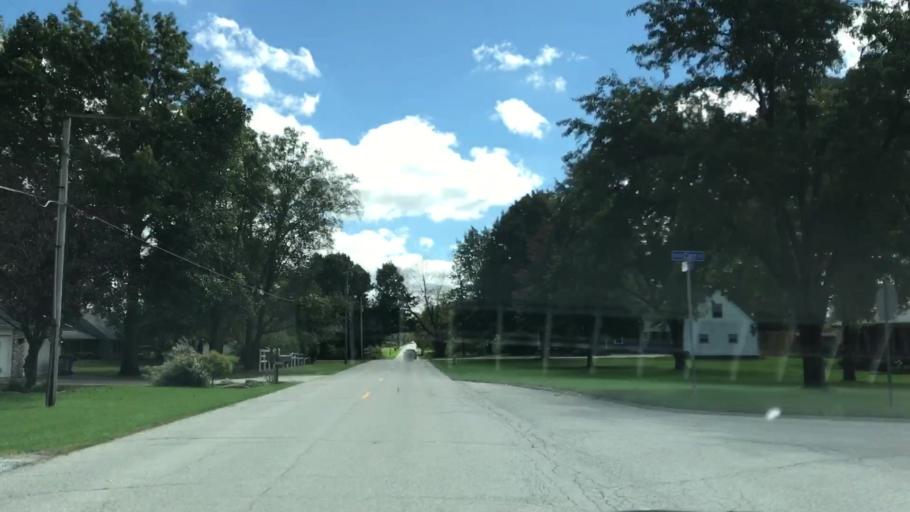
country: US
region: Indiana
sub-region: Howard County
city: Indian Heights
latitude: 40.4301
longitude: -86.1004
